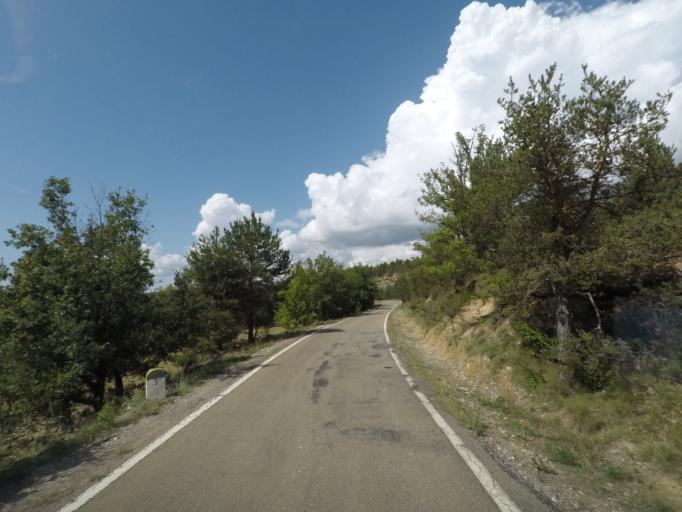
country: ES
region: Aragon
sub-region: Provincia de Huesca
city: Yebra de Basa
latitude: 42.3984
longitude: -0.3536
